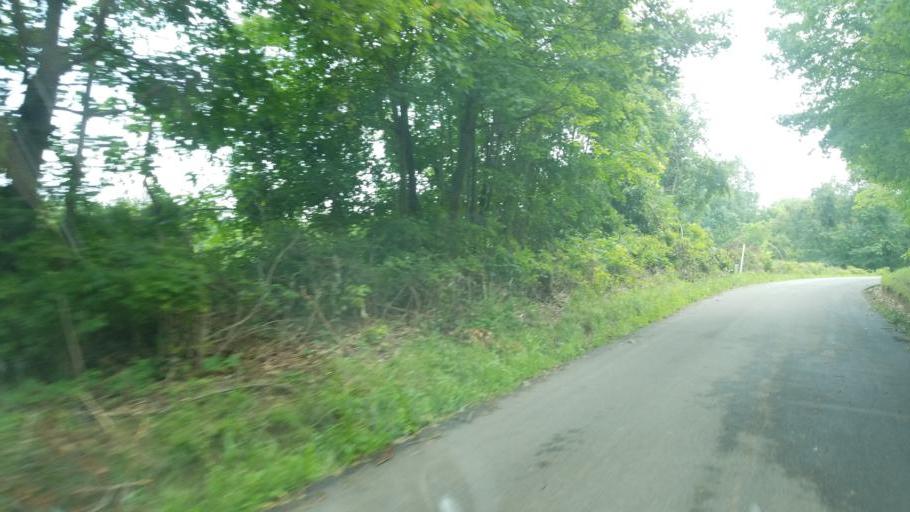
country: US
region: Ohio
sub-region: Licking County
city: Utica
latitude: 40.1855
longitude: -82.4646
